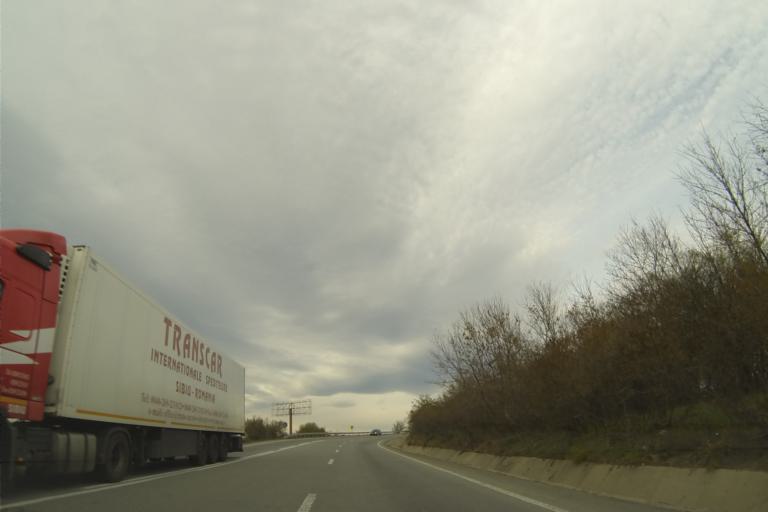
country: RO
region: Olt
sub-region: Comuna Valea Mare
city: Valea Mare
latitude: 44.4880
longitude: 24.4425
